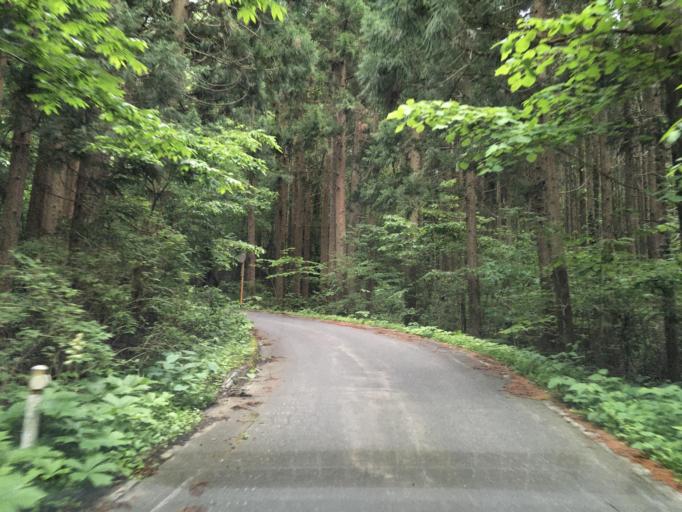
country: JP
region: Iwate
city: Mizusawa
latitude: 39.1256
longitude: 141.2895
